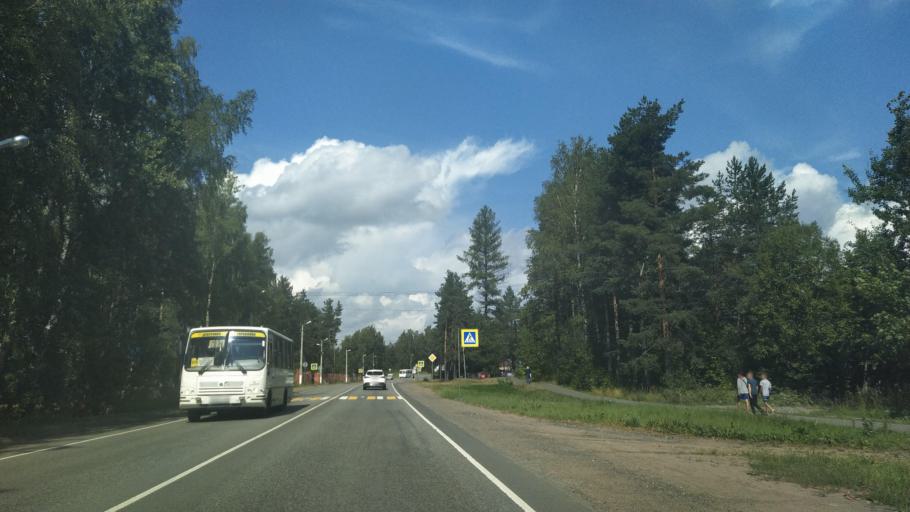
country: RU
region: Leningrad
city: Toksovo
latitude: 60.1497
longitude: 30.5224
